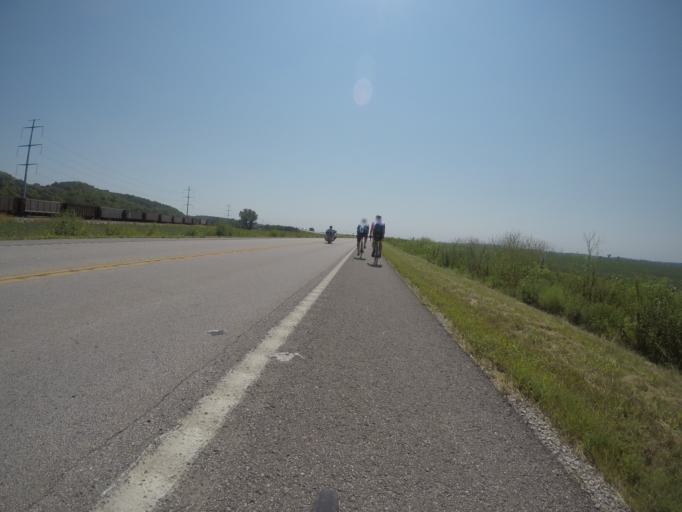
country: US
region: Missouri
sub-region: Platte County
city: Weston
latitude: 39.4431
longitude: -94.9483
